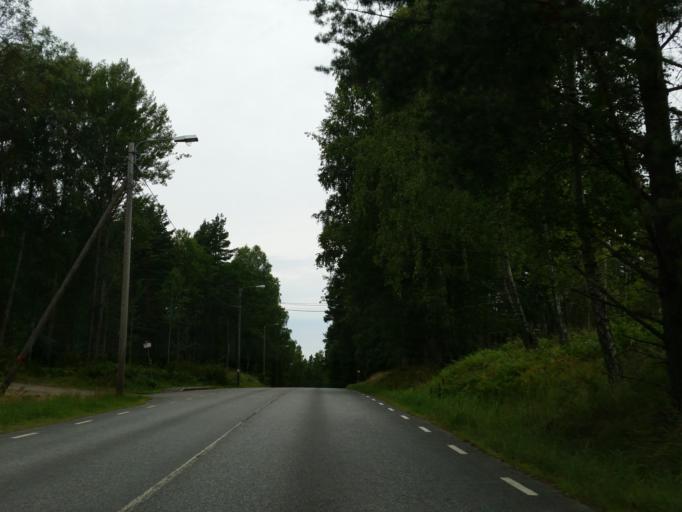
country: SE
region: Stockholm
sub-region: Sodertalje Kommun
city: Soedertaelje
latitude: 59.1993
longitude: 17.5773
